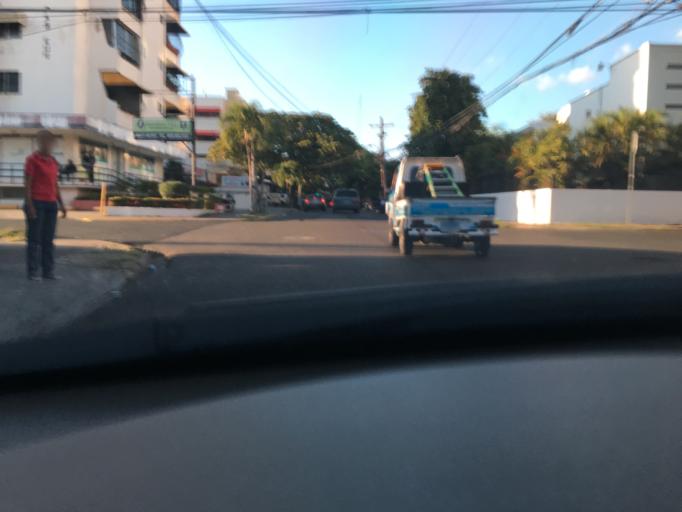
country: DO
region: Nacional
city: Ciudad Nueva
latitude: 18.4689
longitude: -69.9000
